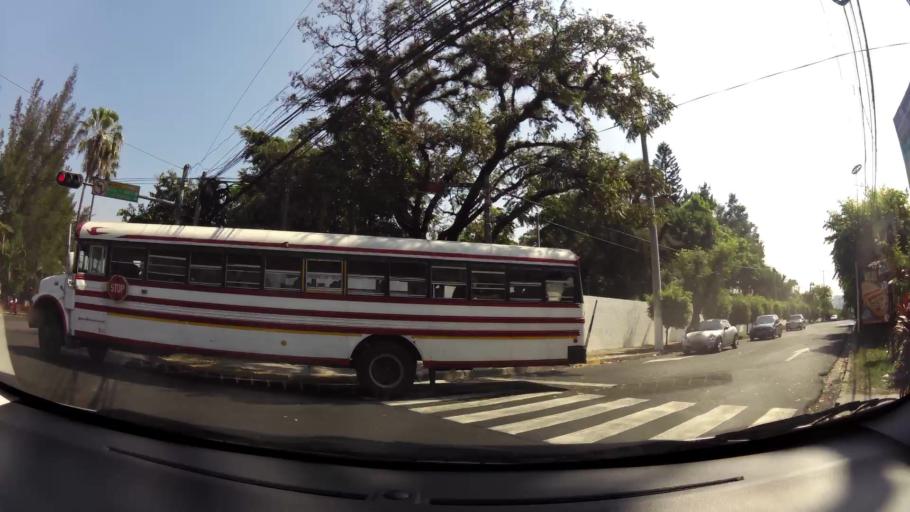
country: SV
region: La Libertad
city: Antiguo Cuscatlan
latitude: 13.6899
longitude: -89.2320
